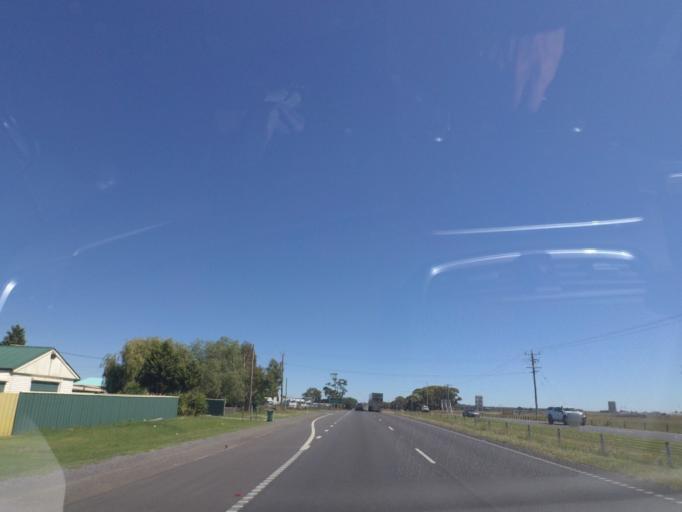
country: AU
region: Victoria
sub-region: Hume
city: Craigieburn
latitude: -37.5299
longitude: 144.9474
